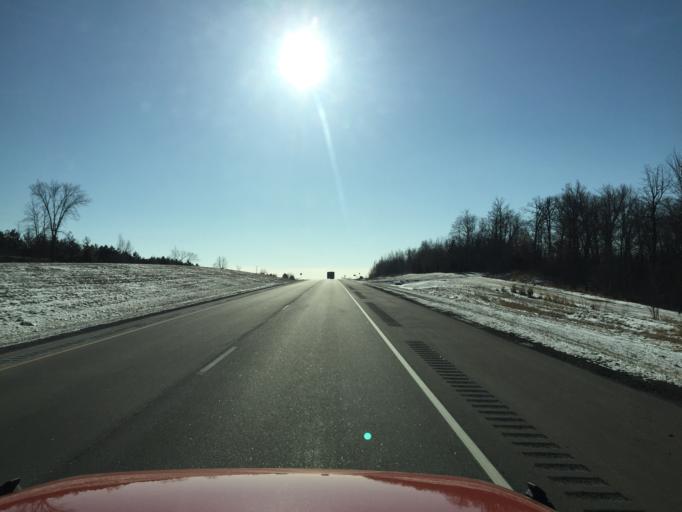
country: US
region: Minnesota
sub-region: Mille Lacs County
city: Milaca
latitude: 45.8126
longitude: -93.6553
